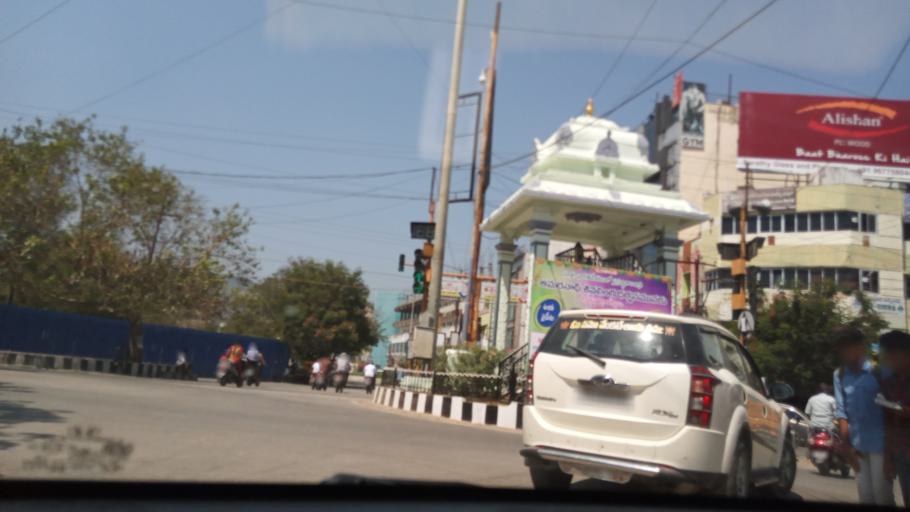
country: IN
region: Andhra Pradesh
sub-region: Chittoor
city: Tirupati
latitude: 13.6224
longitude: 79.4178
